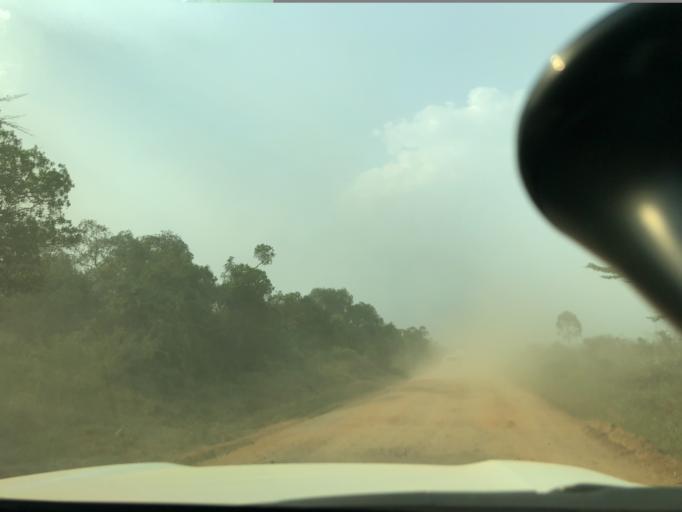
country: CD
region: Nord Kivu
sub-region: North Kivu
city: Butembo
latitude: 0.1062
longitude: 29.6399
